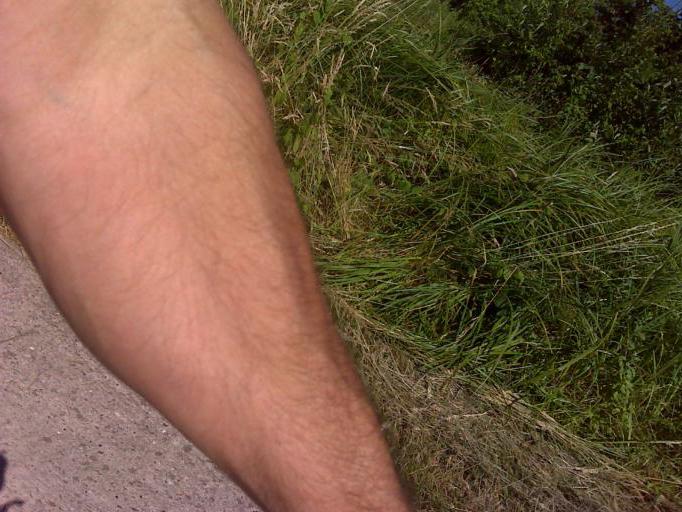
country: FR
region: Picardie
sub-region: Departement de la Somme
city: Quend
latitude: 50.3170
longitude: 1.5969
